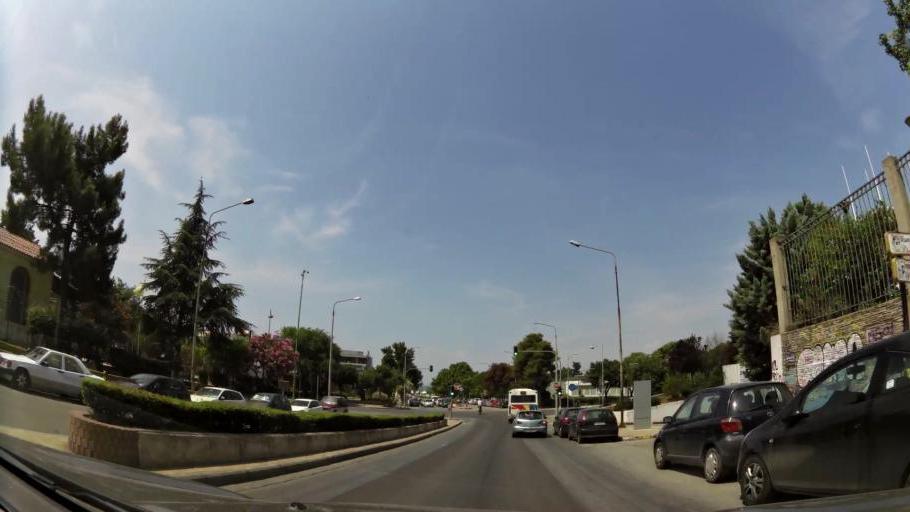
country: GR
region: Central Macedonia
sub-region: Nomos Thessalonikis
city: Agios Pavlos
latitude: 40.6251
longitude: 22.9555
